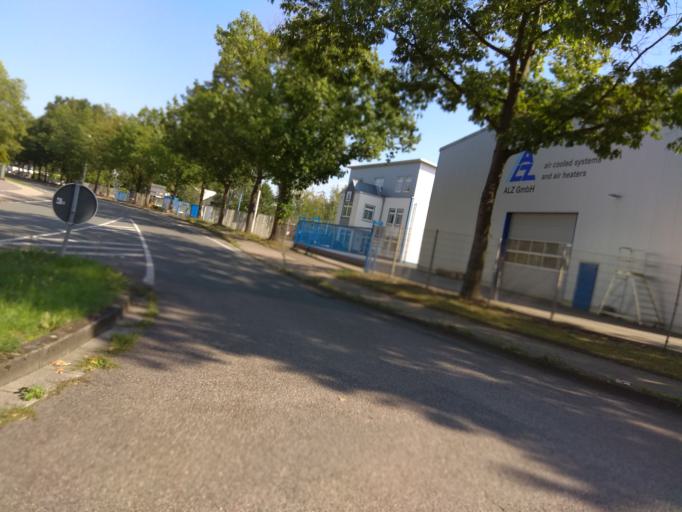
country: DE
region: North Rhine-Westphalia
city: Dorsten
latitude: 51.7147
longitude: 7.0033
